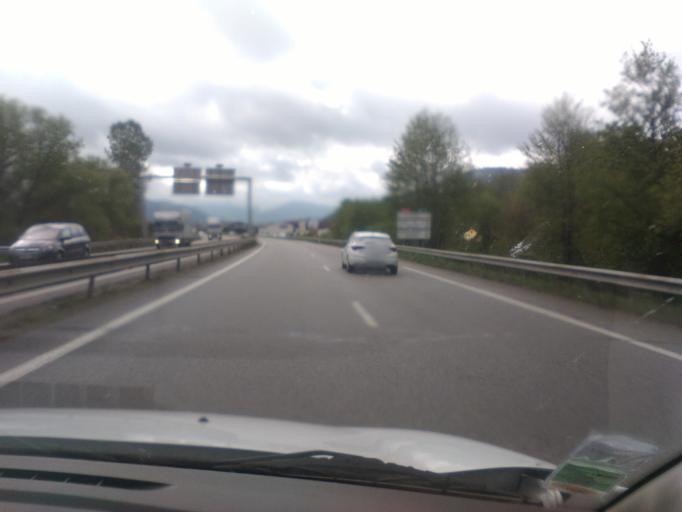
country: FR
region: Lorraine
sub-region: Departement des Vosges
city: Remiremont
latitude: 48.0290
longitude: 6.5830
